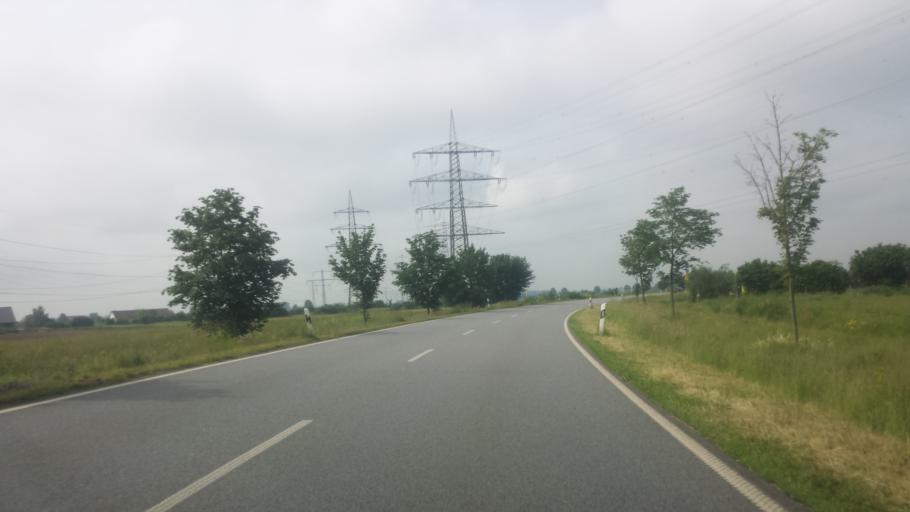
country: DE
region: Hesse
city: Pfungstadt
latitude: 49.8069
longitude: 8.5856
